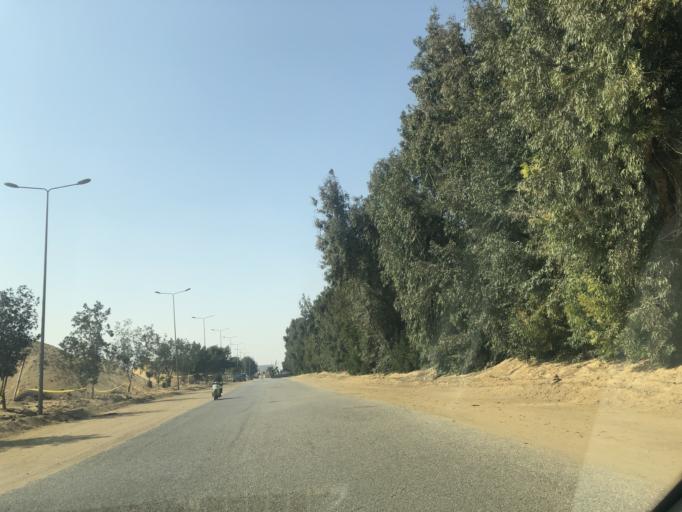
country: EG
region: Al Jizah
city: Madinat Sittah Uktubar
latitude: 29.9608
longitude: 31.0046
